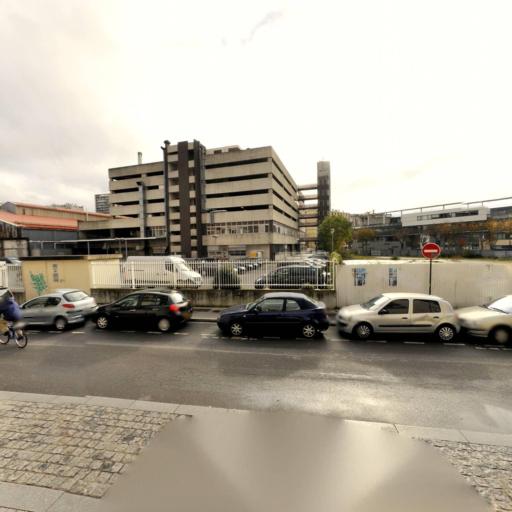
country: FR
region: Ile-de-France
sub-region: Departement des Hauts-de-Seine
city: Boulogne-Billancourt
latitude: 48.8273
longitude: 2.2445
